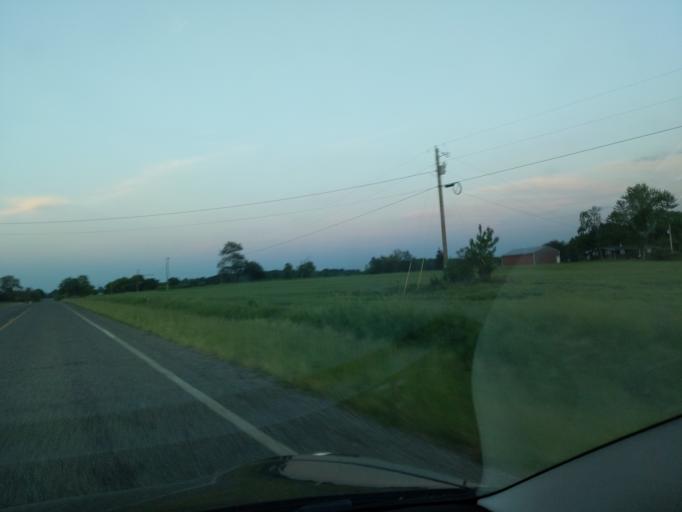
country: US
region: Michigan
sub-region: Barry County
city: Nashville
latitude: 42.5383
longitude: -85.0504
